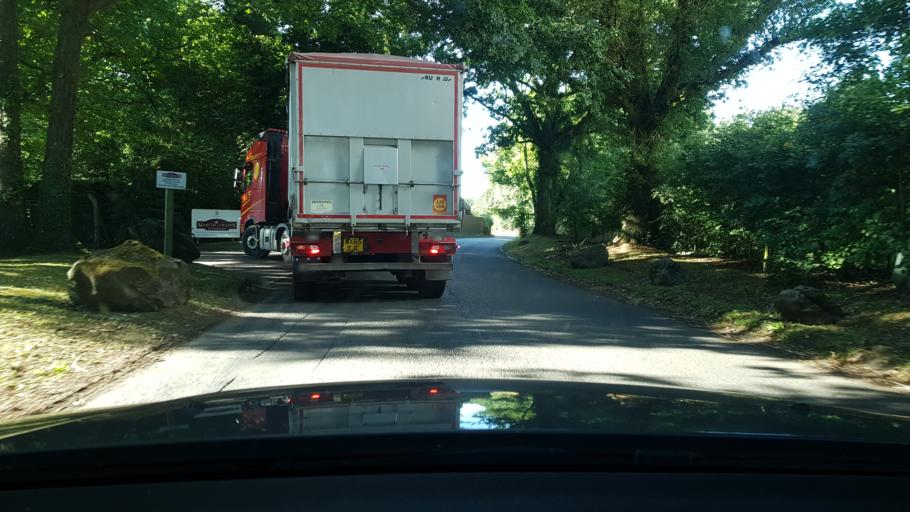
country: GB
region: England
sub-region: West Berkshire
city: Lambourn
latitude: 51.4761
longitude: -1.5520
